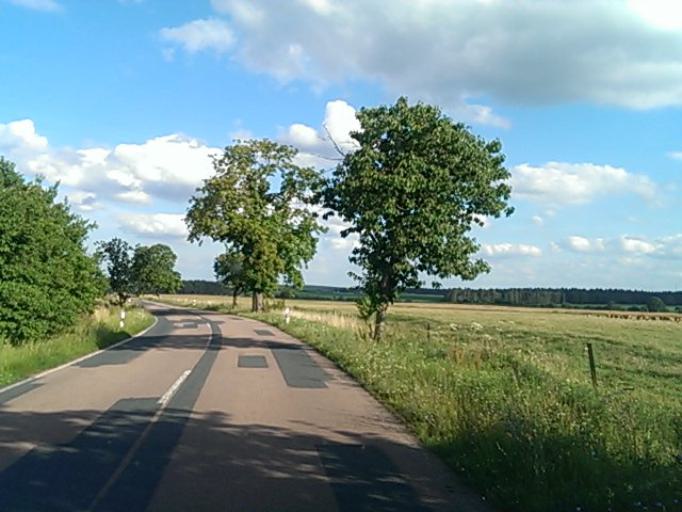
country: DE
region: Saxony-Anhalt
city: Nudersdorf
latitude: 51.9662
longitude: 12.5730
